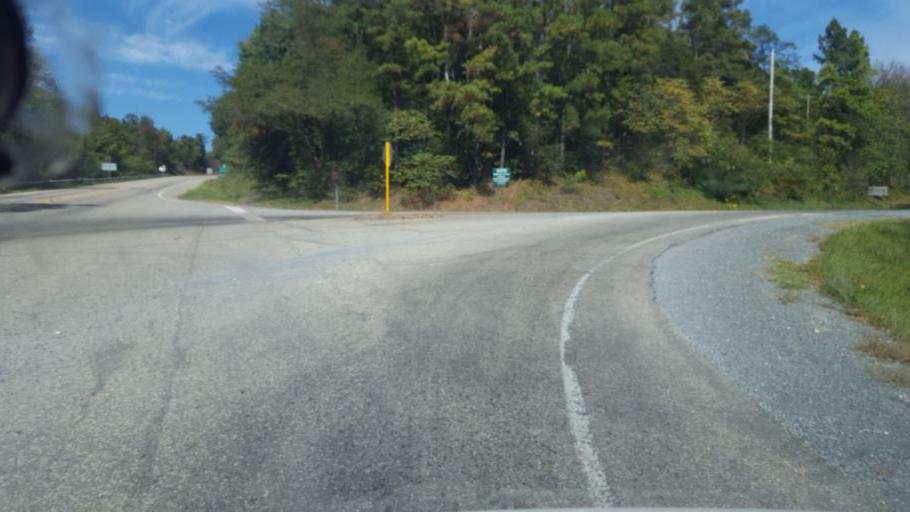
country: US
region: Virginia
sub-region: Page County
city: Stanley
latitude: 38.5891
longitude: -78.5912
